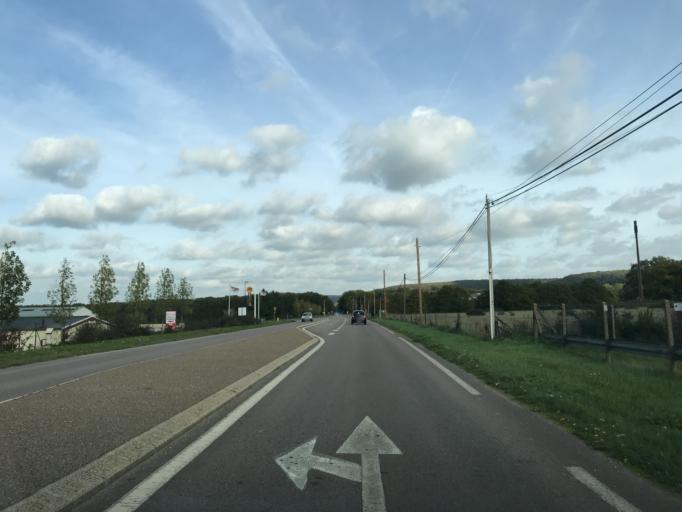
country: FR
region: Haute-Normandie
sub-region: Departement de l'Eure
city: Courcelles-sur-Seine
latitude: 49.1897
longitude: 1.3676
